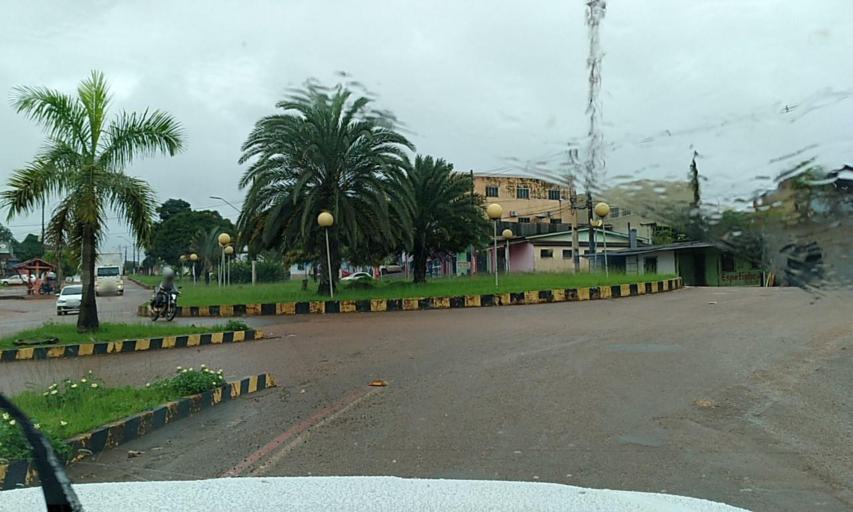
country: BR
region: Para
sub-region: Altamira
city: Altamira
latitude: -3.2127
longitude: -52.2323
